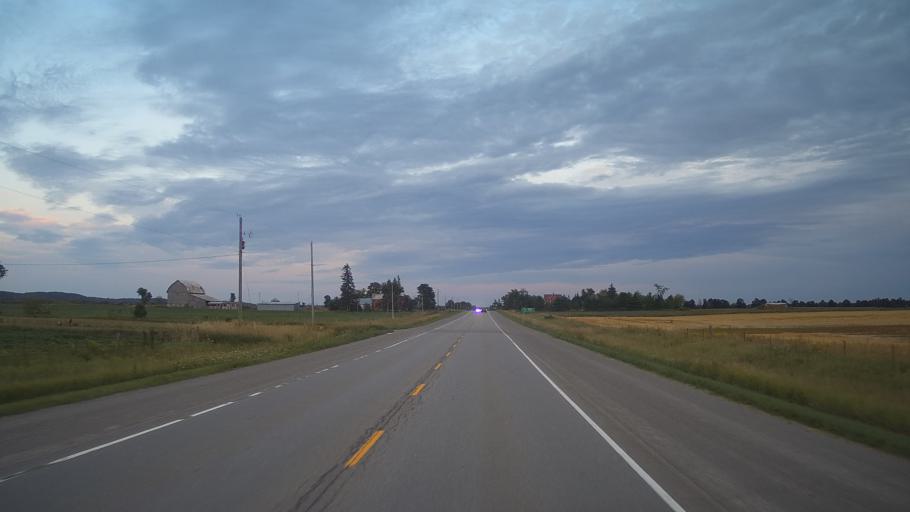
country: CA
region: Ontario
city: Pembroke
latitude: 45.7038
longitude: -76.9696
